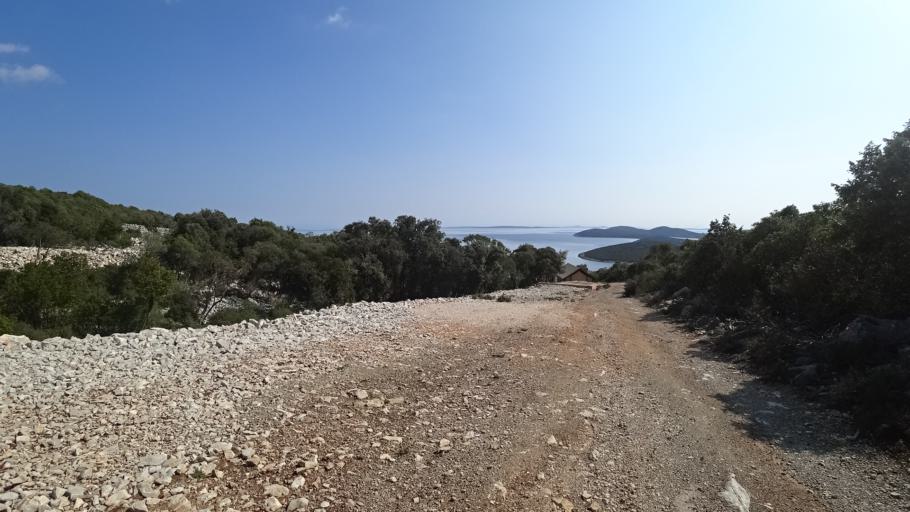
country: HR
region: Primorsko-Goranska
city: Mali Losinj
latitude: 44.4873
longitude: 14.5359
